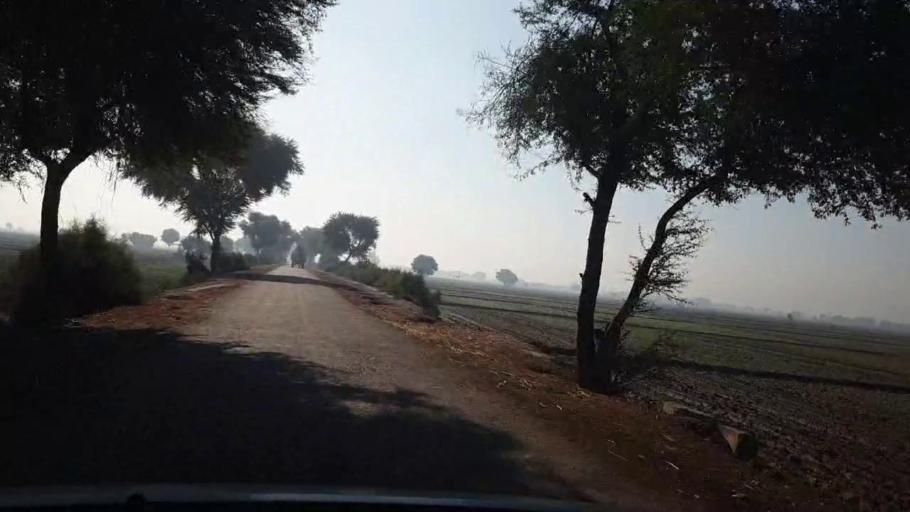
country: PK
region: Sindh
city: Dadu
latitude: 26.6675
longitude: 67.8162
